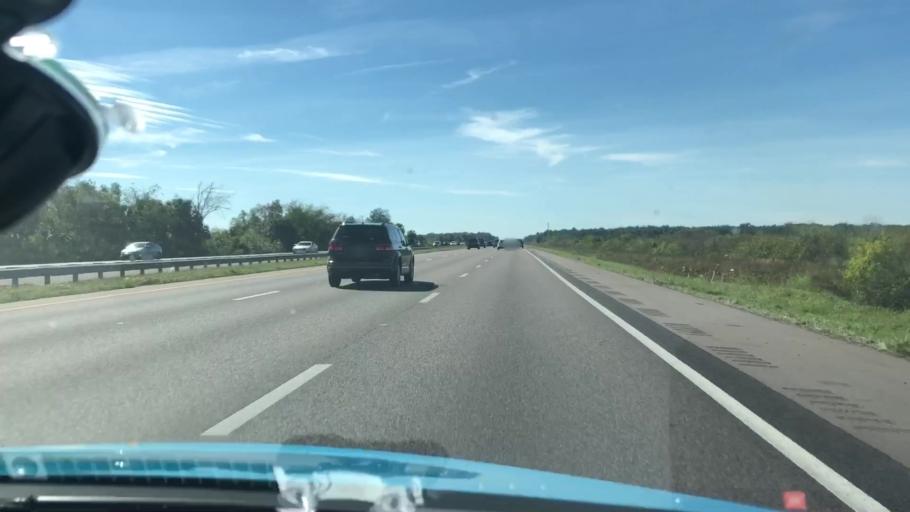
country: US
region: Florida
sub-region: Volusia County
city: DeBary
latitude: 28.8567
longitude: -81.2983
